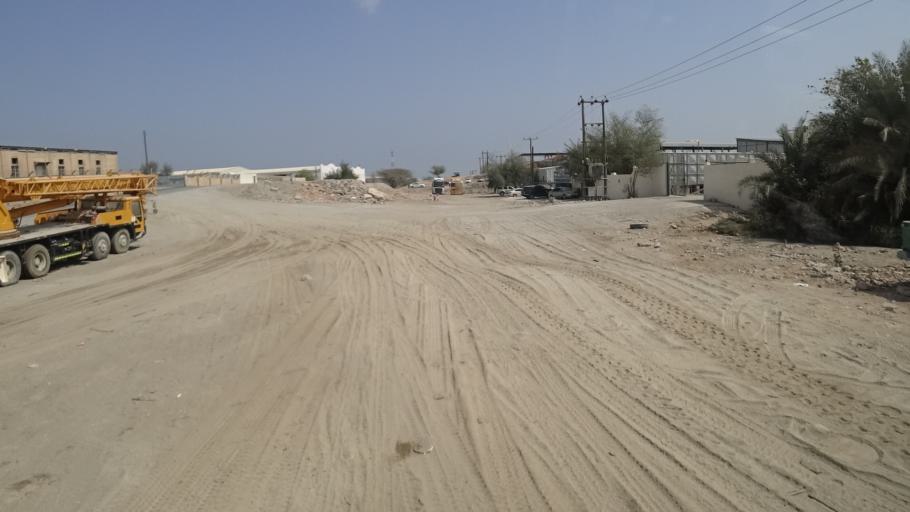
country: OM
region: Muhafazat Masqat
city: Bawshar
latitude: 23.5720
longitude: 58.3461
